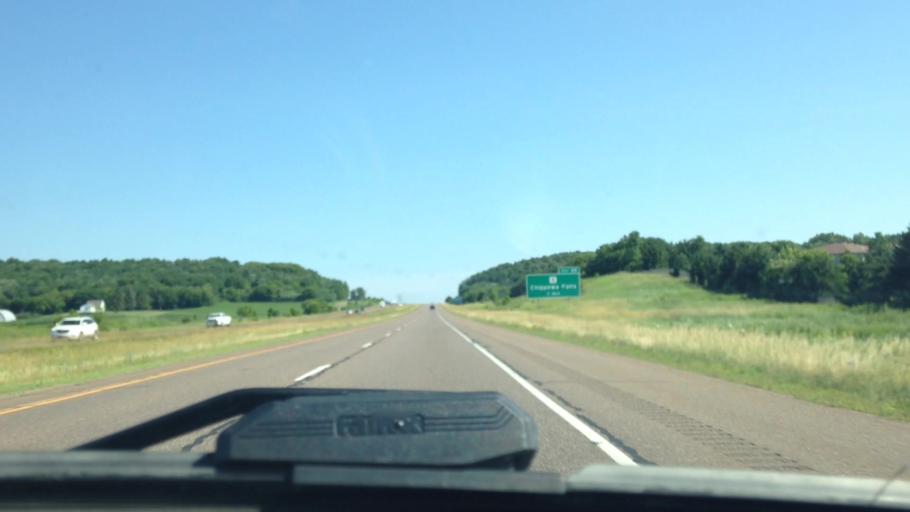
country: US
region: Wisconsin
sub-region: Chippewa County
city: Chippewa Falls
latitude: 44.9461
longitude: -91.4267
